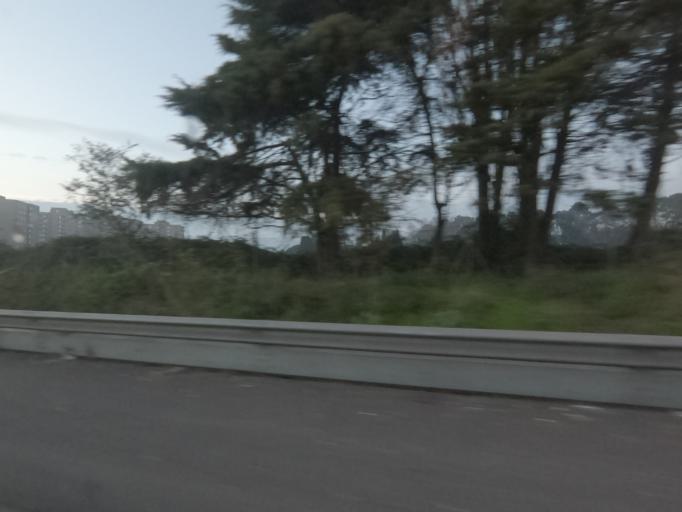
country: PT
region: Porto
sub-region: Matosinhos
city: Senhora da Hora
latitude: 41.1723
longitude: -8.6309
